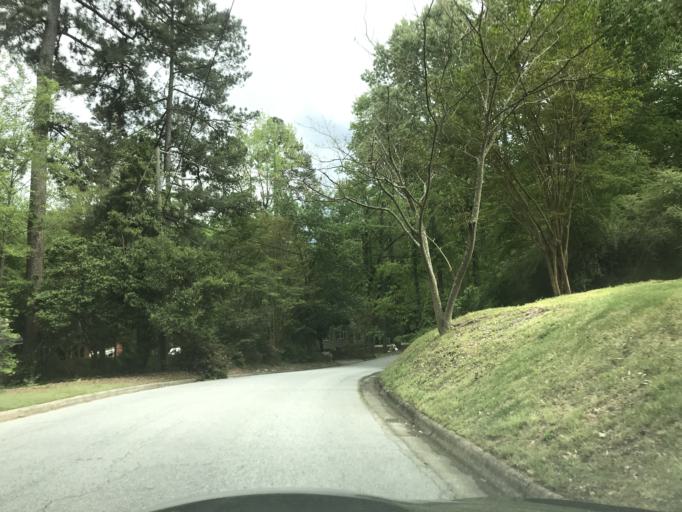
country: US
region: North Carolina
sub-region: Wake County
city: Raleigh
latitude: 35.7831
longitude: -78.5966
